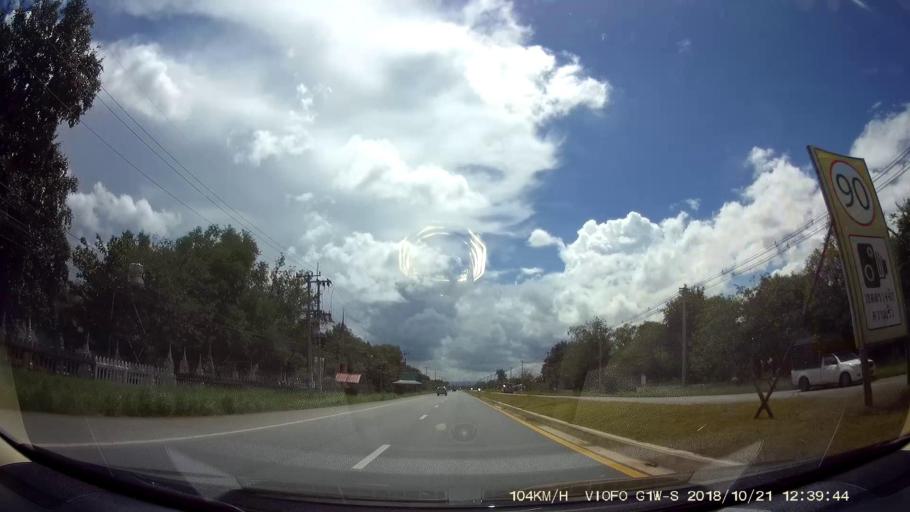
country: TH
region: Nakhon Ratchasima
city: Amphoe Sikhiu
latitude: 15.0349
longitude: 101.6992
